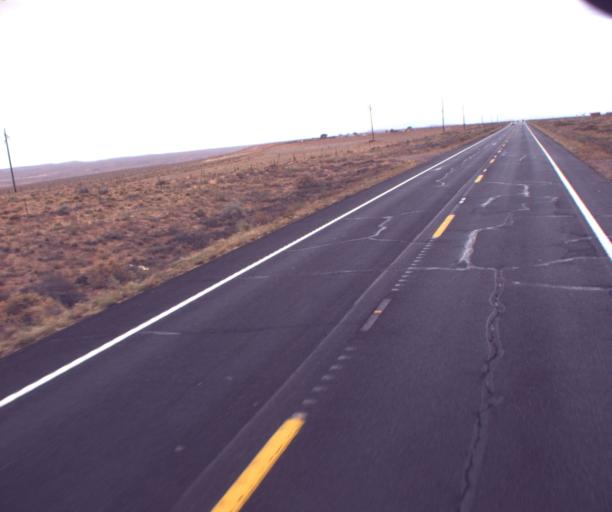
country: US
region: Arizona
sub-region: Coconino County
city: Tuba City
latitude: 36.1488
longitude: -111.1388
